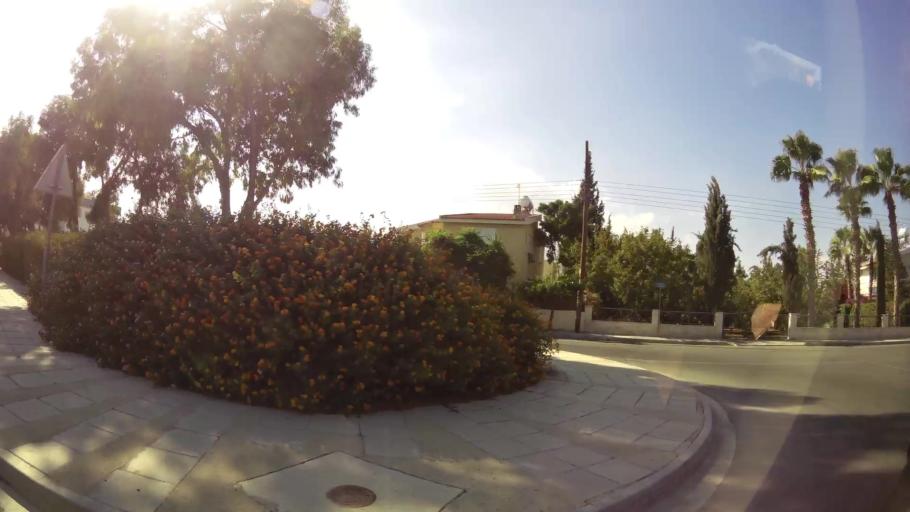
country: CY
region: Larnaka
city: Livadia
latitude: 34.9434
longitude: 33.6319
